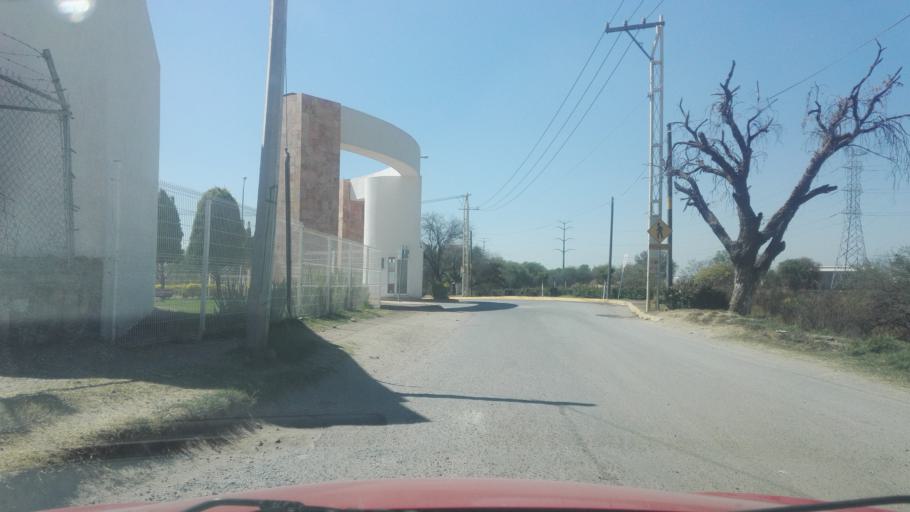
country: MX
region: Guanajuato
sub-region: Leon
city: Fraccionamiento Paraiso Real
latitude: 21.0852
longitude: -101.5921
